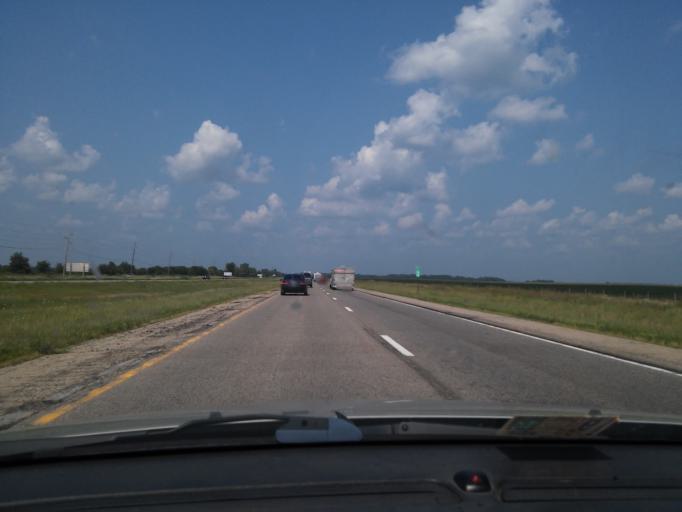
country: US
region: Illinois
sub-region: Logan County
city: Lincoln
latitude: 40.2024
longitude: -89.2989
